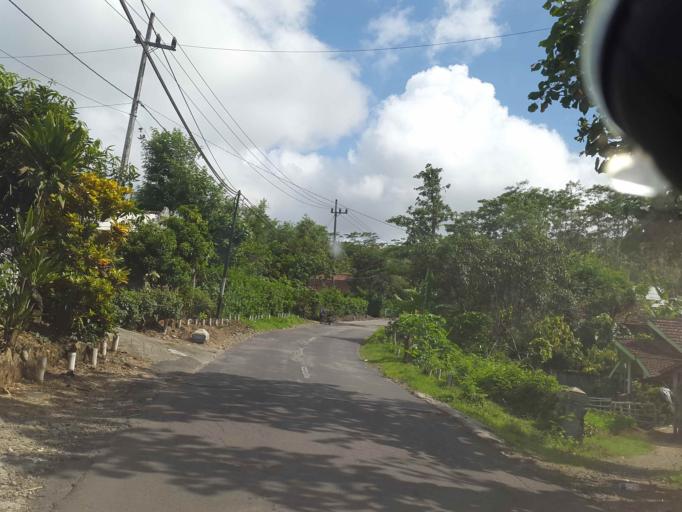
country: ID
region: East Java
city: Binangun
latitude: -8.2356
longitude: 112.3363
